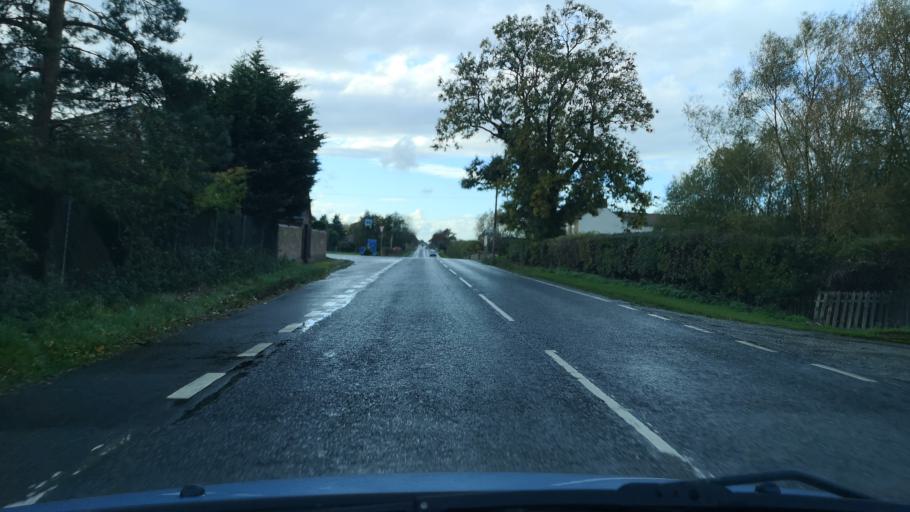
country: GB
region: England
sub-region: Doncaster
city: Hatfield
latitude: 53.5873
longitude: -0.9169
